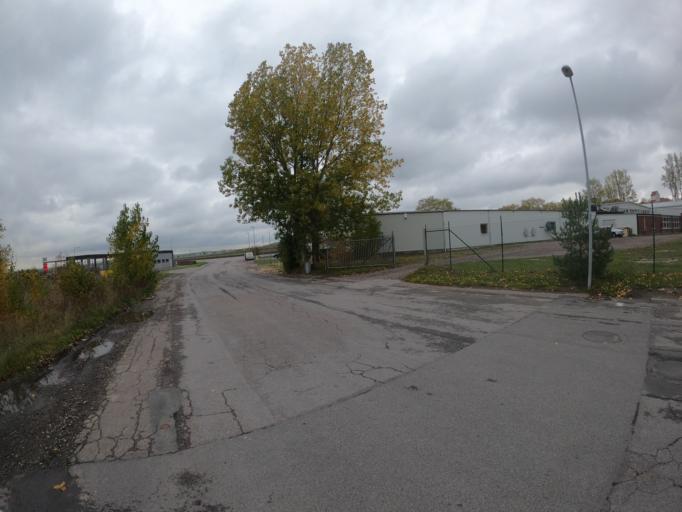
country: SE
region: Skane
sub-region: Lunds Kommun
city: Genarp
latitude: 55.6615
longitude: 13.3389
